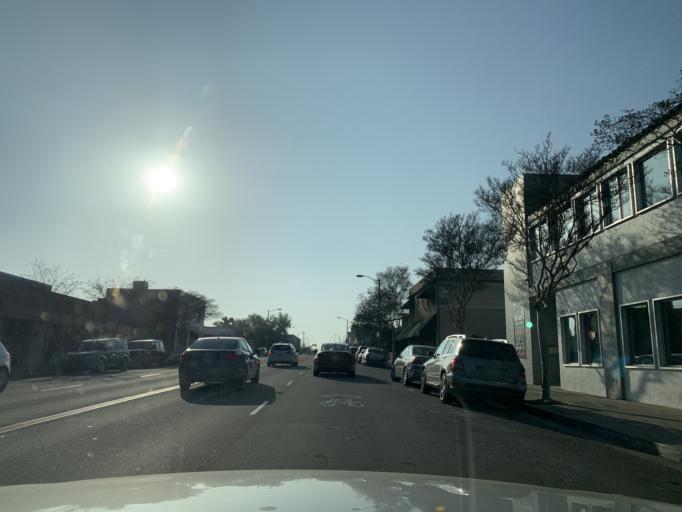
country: US
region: California
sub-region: Los Angeles County
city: South Pasadena
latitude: 34.1158
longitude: -118.1539
